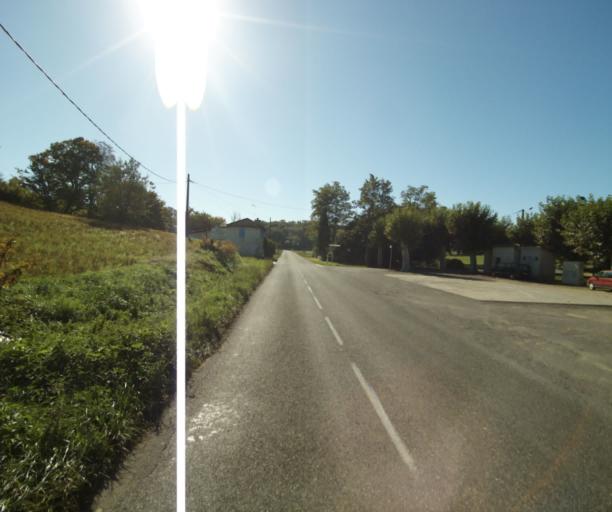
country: FR
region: Midi-Pyrenees
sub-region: Departement du Gers
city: Gondrin
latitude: 43.8147
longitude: 0.1866
